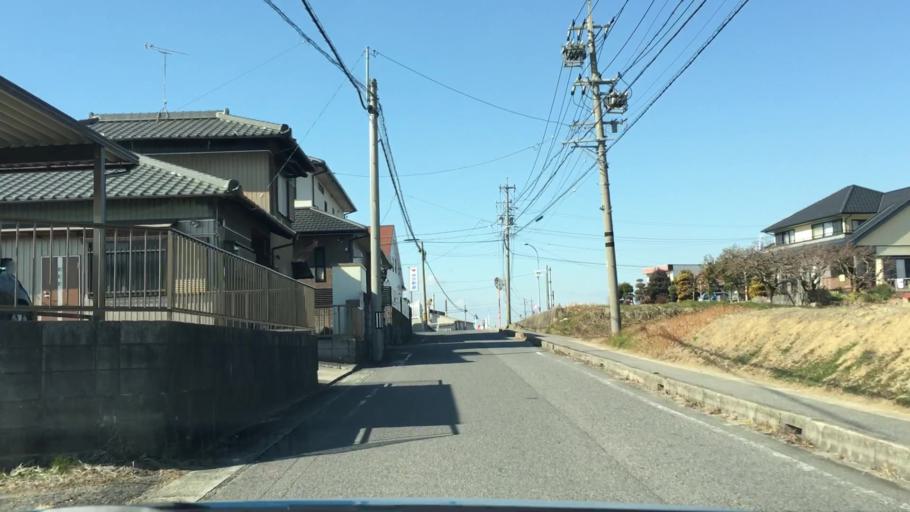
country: JP
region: Aichi
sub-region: Toyota-shi
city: Toyota
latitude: 35.0343
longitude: 137.1251
